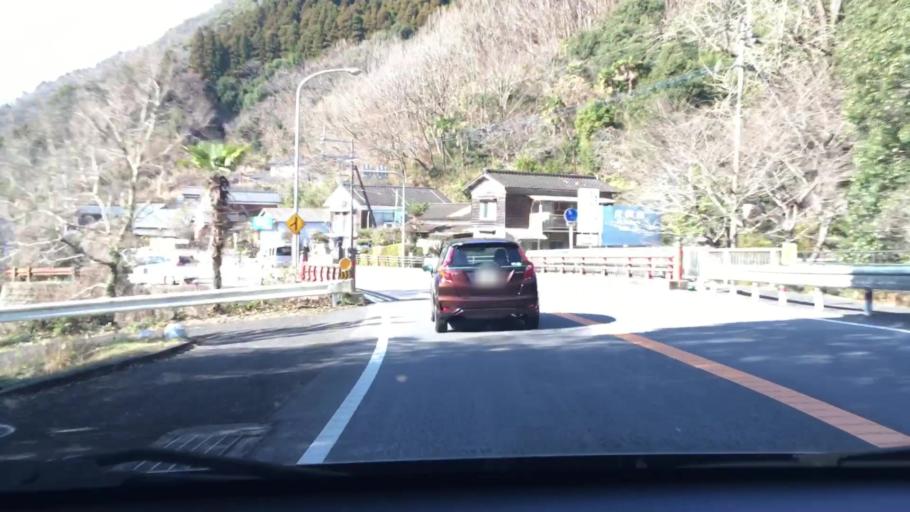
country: JP
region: Oita
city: Saiki
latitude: 32.9949
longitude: 131.8278
